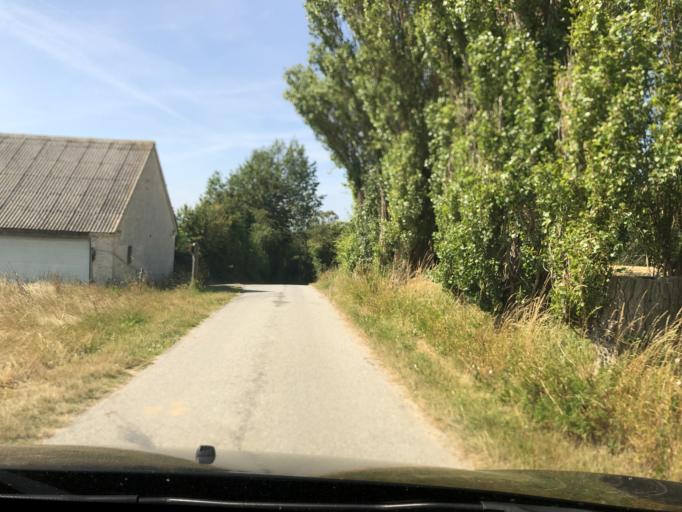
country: DK
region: South Denmark
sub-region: AEro Kommune
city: AEroskobing
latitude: 54.9023
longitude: 10.2787
